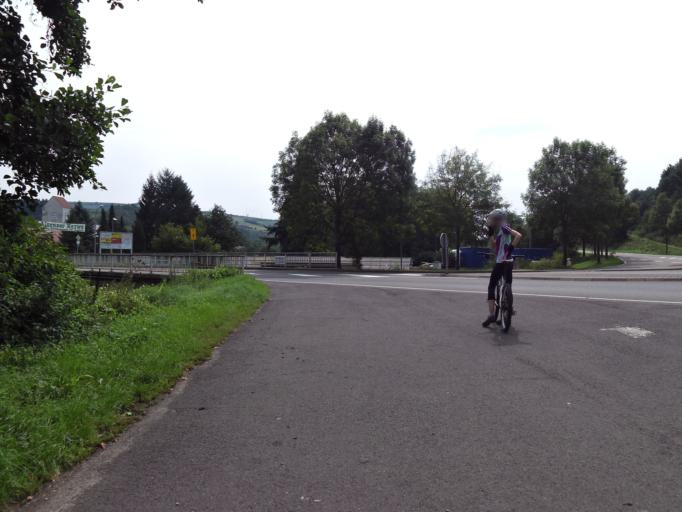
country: DE
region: Rheinland-Pfalz
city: Niedermoschel
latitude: 49.7324
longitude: 7.8144
